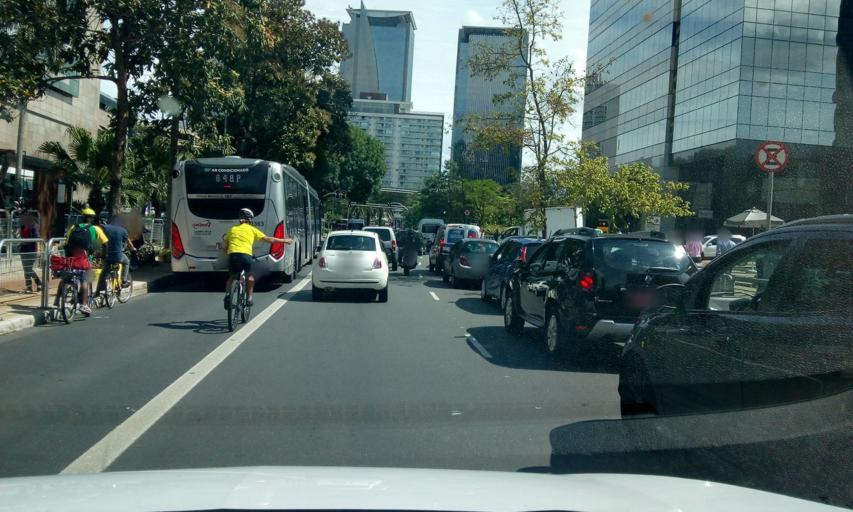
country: BR
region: Sao Paulo
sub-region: Taboao Da Serra
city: Taboao da Serra
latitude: -23.6231
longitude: -46.6995
